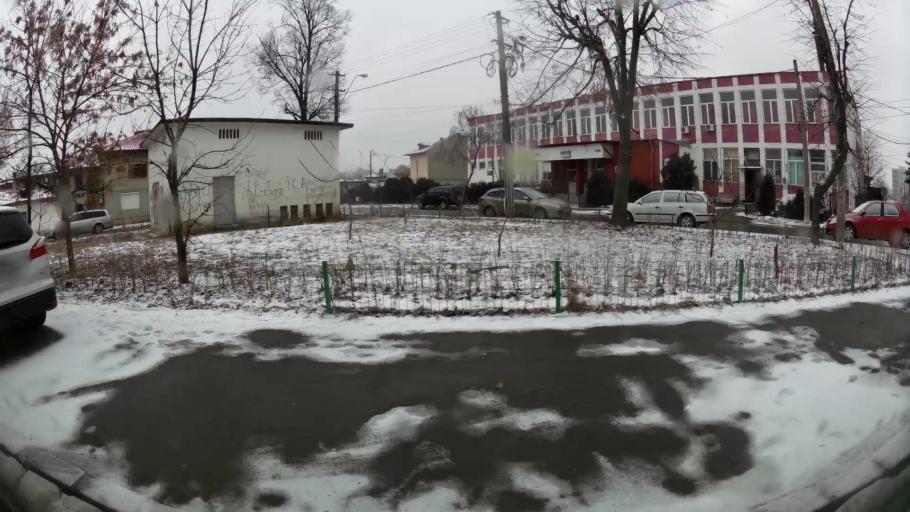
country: RO
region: Prahova
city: Ploiesti
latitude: 44.9477
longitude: 26.0281
